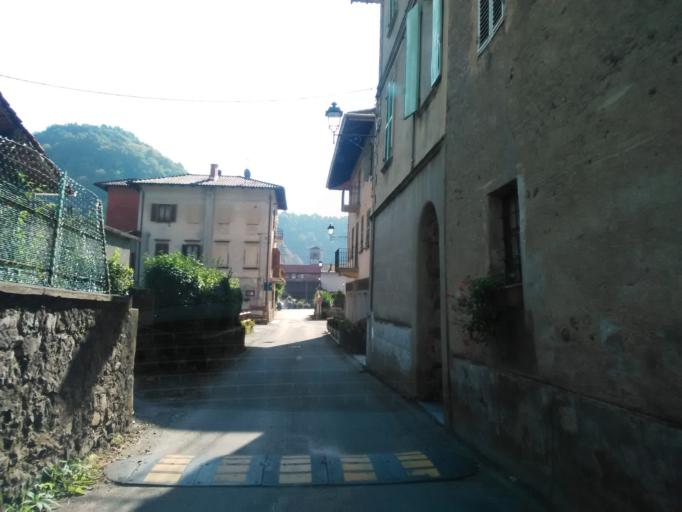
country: IT
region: Piedmont
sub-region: Provincia di Vercelli
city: Postua
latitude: 45.7151
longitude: 8.2284
